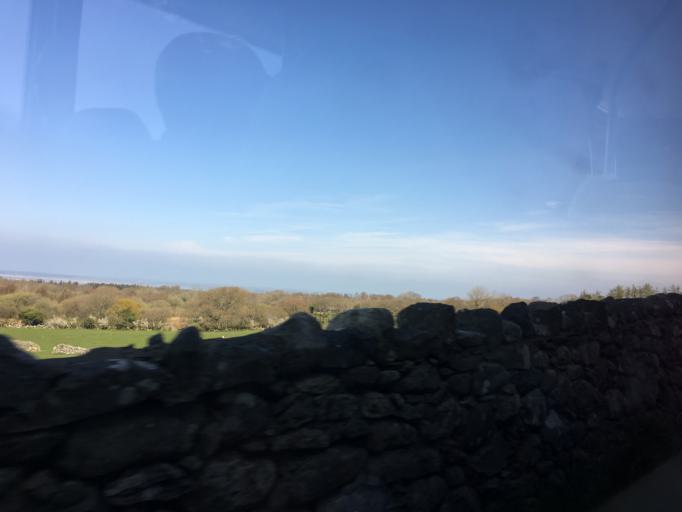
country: GB
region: Wales
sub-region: Gwynedd
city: Llanwnda
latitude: 53.0613
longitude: -4.2792
